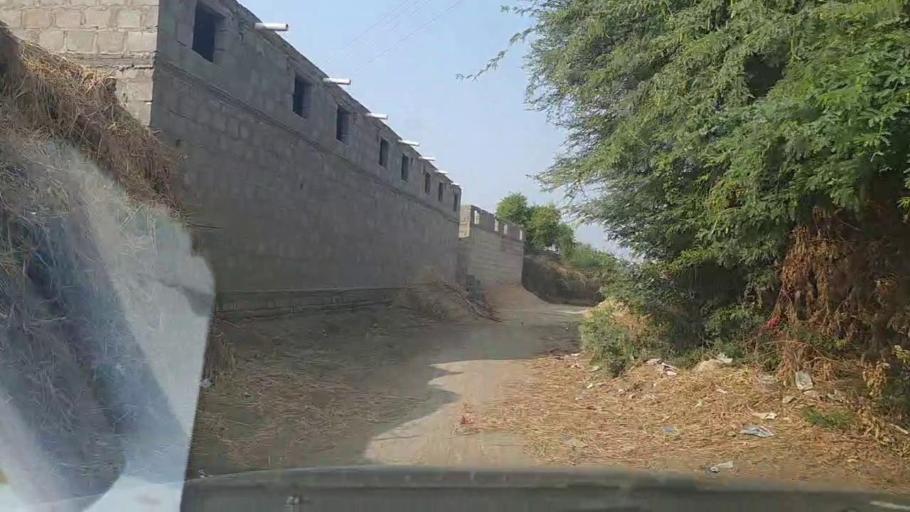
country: PK
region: Sindh
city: Bulri
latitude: 24.9406
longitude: 68.2790
